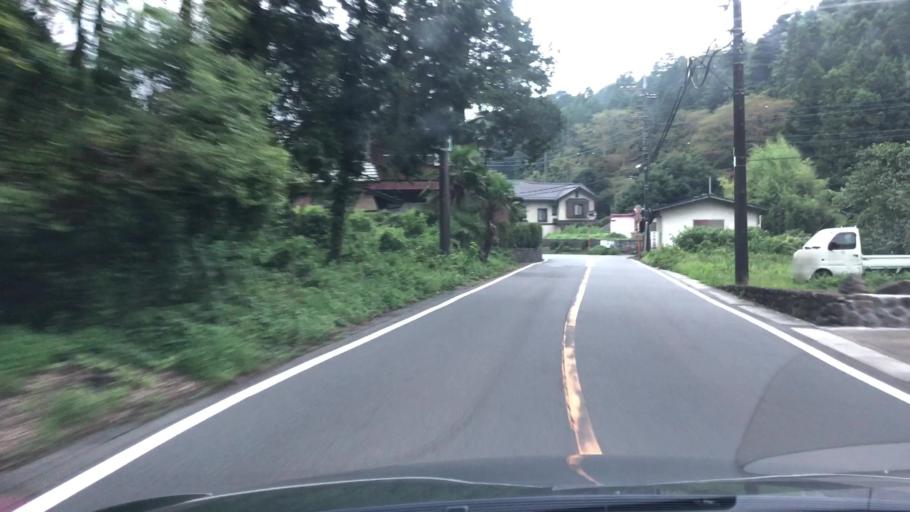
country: JP
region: Tokyo
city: Ome
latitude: 35.7621
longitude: 139.2297
